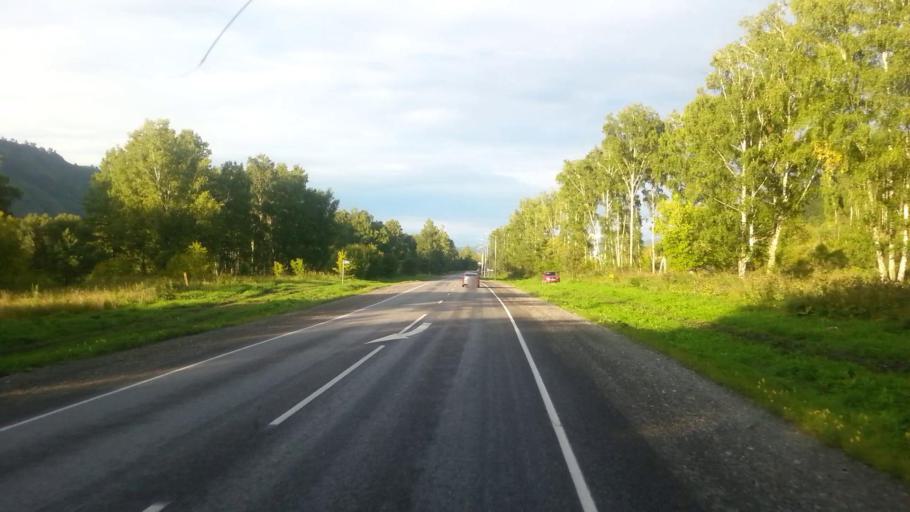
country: RU
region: Altay
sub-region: Mayminskiy Rayon
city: Manzherok
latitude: 51.8667
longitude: 85.7711
